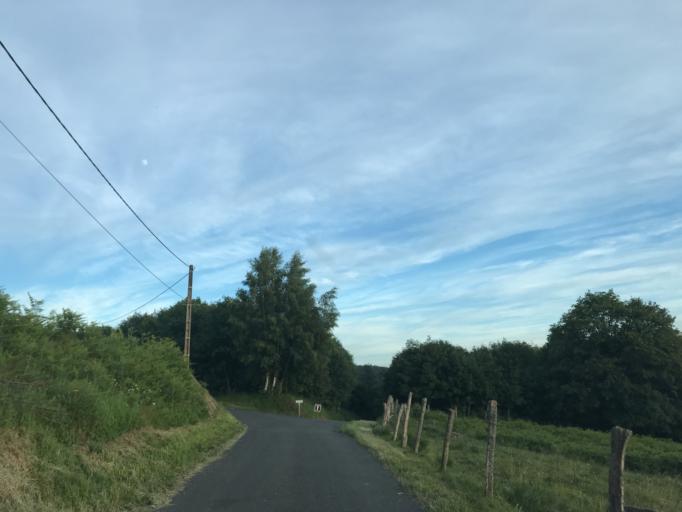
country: FR
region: Rhone-Alpes
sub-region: Departement de la Loire
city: Noiretable
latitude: 45.7714
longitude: 3.7071
